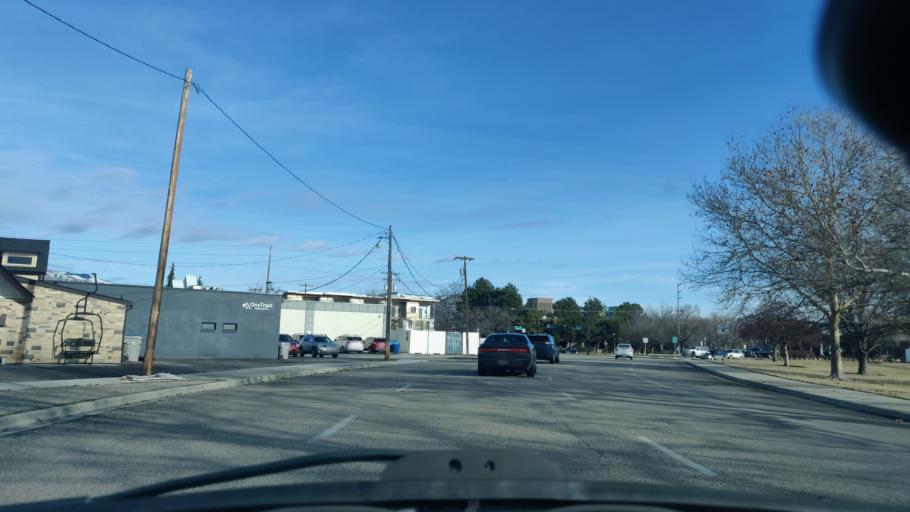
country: US
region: Idaho
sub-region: Ada County
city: Boise
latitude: 43.6173
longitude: -116.2180
